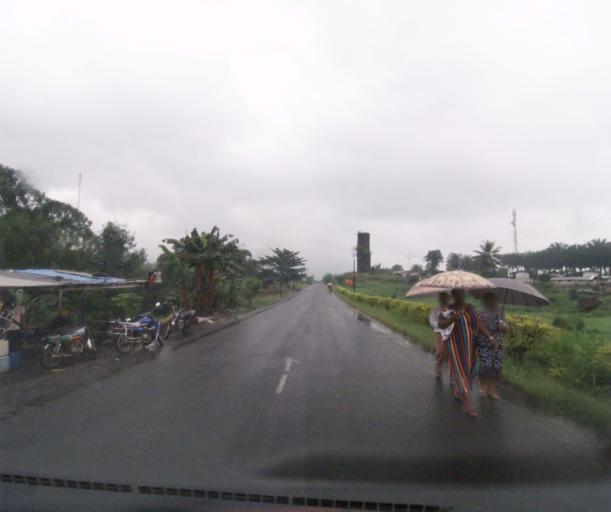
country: CM
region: South-West Province
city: Idenao
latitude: 4.2142
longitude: 8.9890
